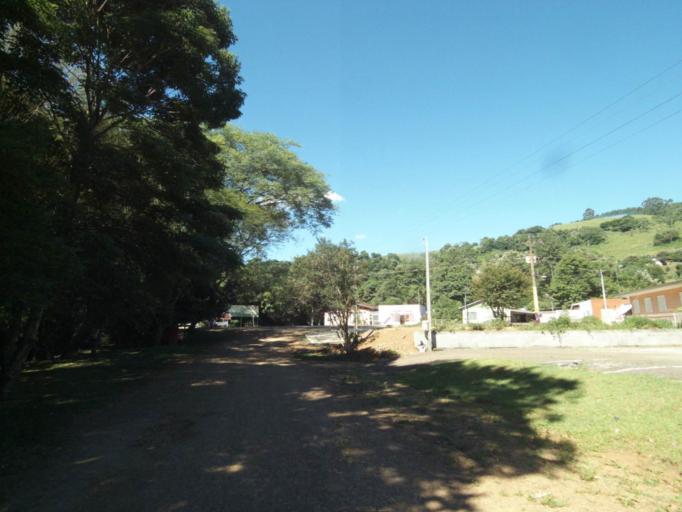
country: BR
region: Parana
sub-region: Ampere
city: Ampere
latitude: -26.1691
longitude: -53.3639
